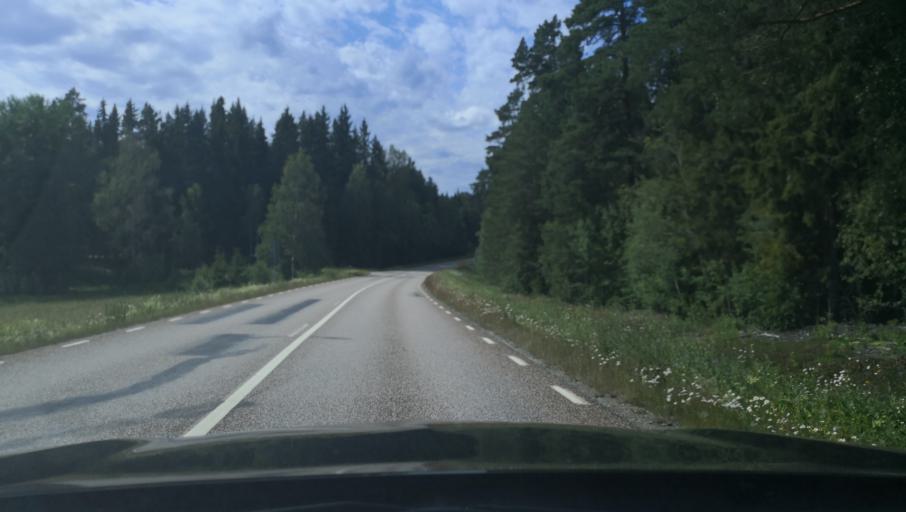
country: SE
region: Dalarna
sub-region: Avesta Kommun
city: Avesta
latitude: 59.9731
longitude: 16.1520
